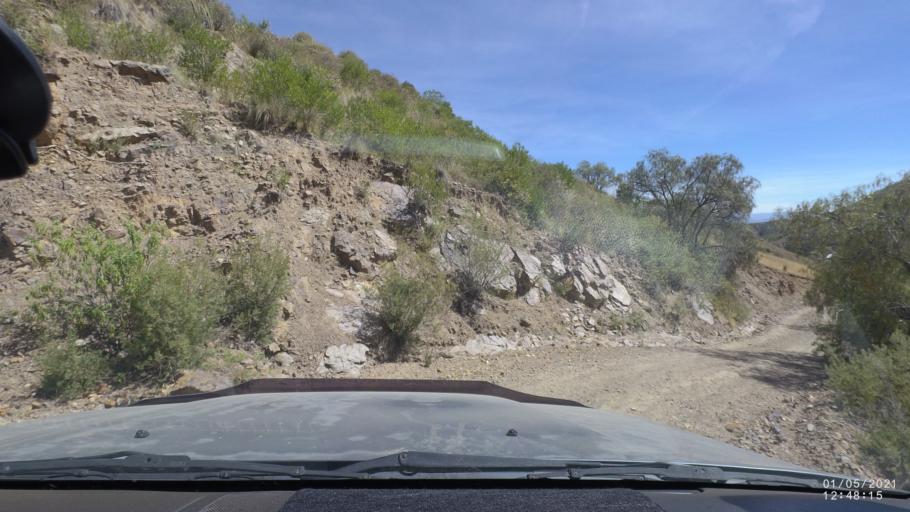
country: BO
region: Cochabamba
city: Capinota
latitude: -17.6869
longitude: -66.1630
